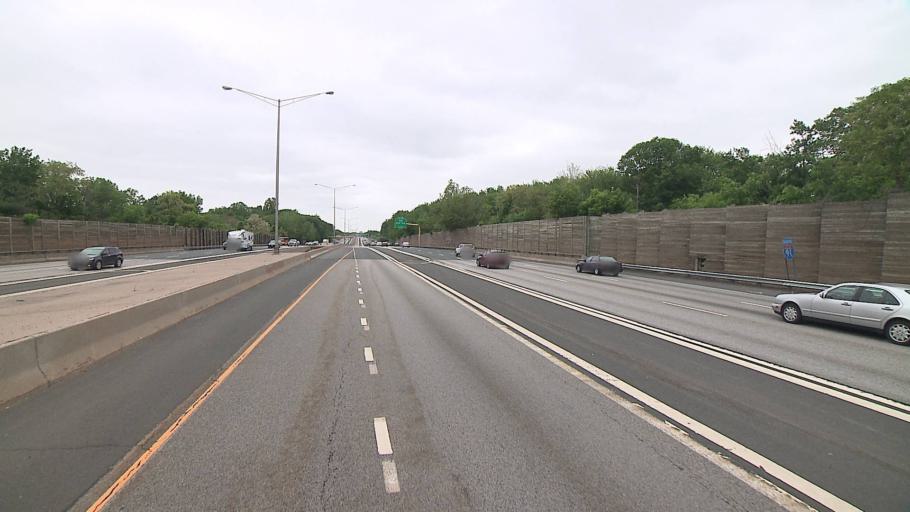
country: US
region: Connecticut
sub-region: Hartford County
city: Windsor
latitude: 41.8471
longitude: -72.6649
